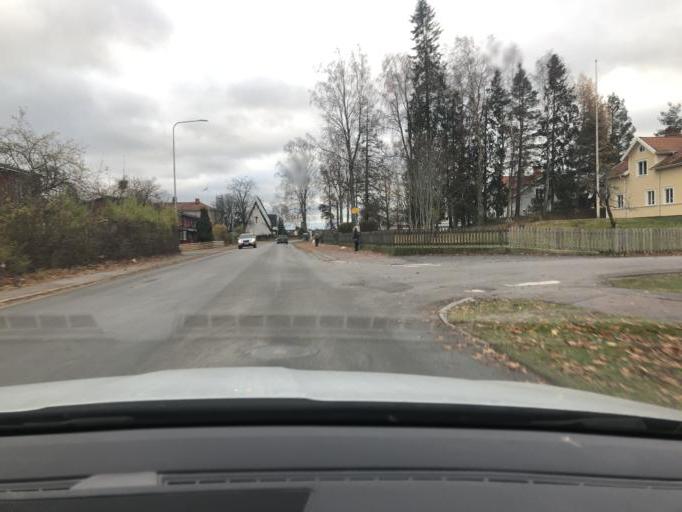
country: SE
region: Uppsala
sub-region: Tierps Kommun
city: Tierp
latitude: 60.3432
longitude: 17.5097
